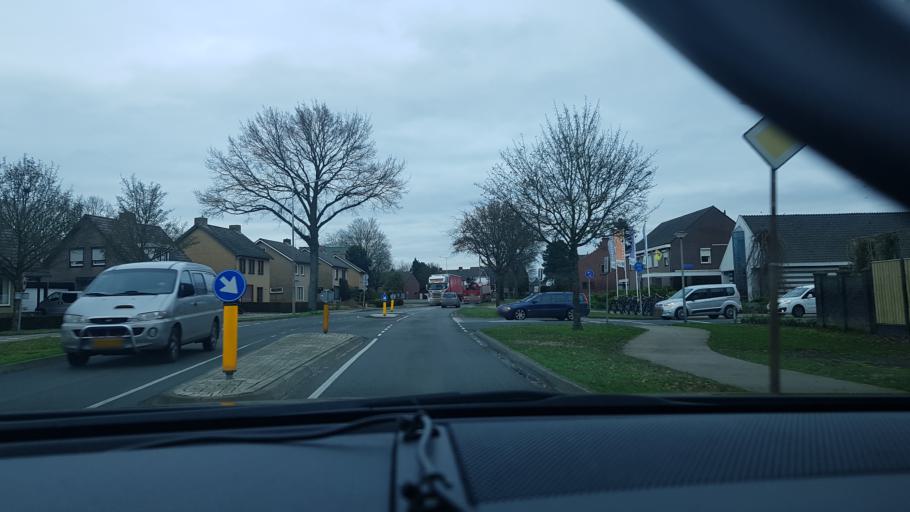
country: NL
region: Limburg
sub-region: Gemeente Leudal
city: Heythuysen
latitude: 51.2602
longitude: 5.9177
